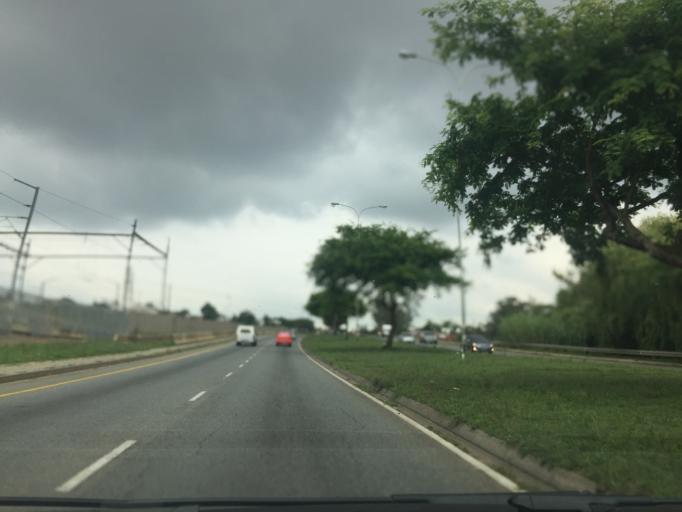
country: ZA
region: Gauteng
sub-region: City of Johannesburg Metropolitan Municipality
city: Modderfontein
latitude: -26.0857
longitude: 28.1013
